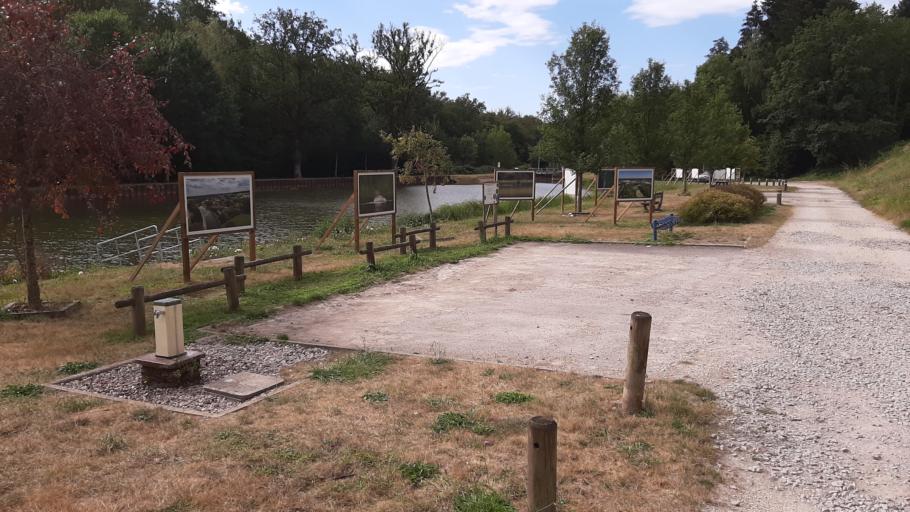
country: FR
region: Lorraine
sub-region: Departement des Vosges
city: Bains-les-Bains
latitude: 48.0149
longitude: 6.2389
